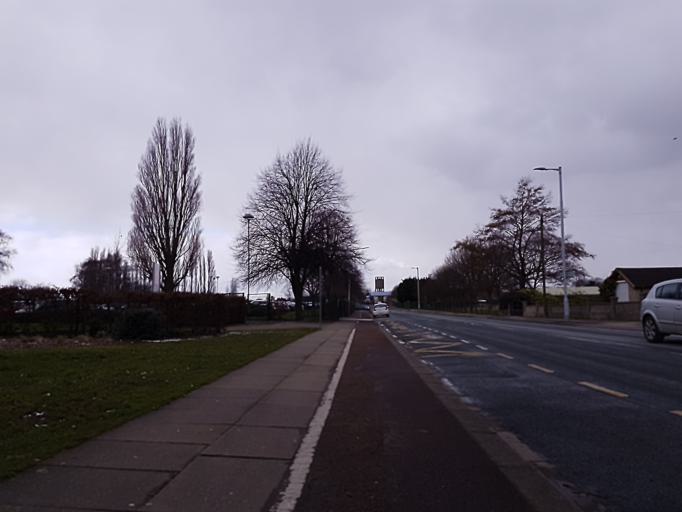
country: GB
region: England
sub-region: North East Lincolnshire
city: Grimbsy
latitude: 53.5562
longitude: -0.0994
